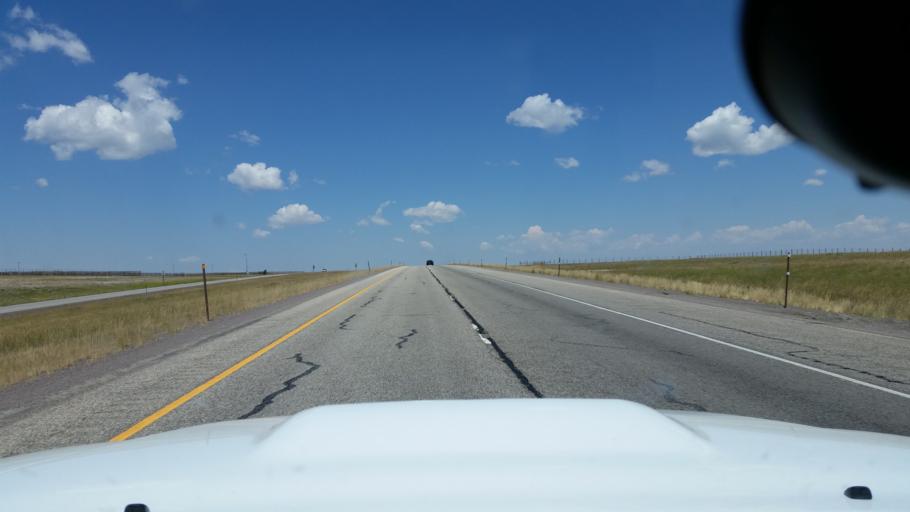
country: US
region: Wyoming
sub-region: Albany County
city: Laramie
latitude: 41.5330
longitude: -106.0728
